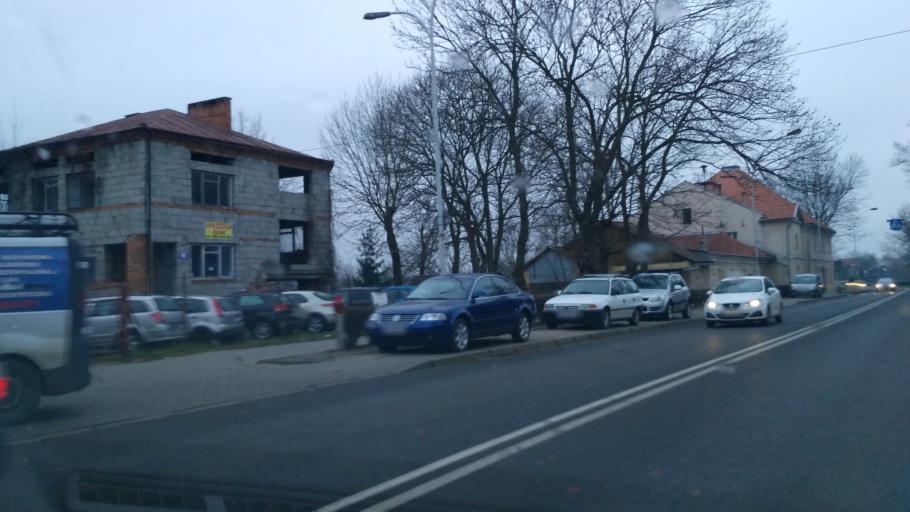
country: PL
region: Subcarpathian Voivodeship
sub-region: Powiat przeworski
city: Przeworsk
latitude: 50.0592
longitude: 22.4874
